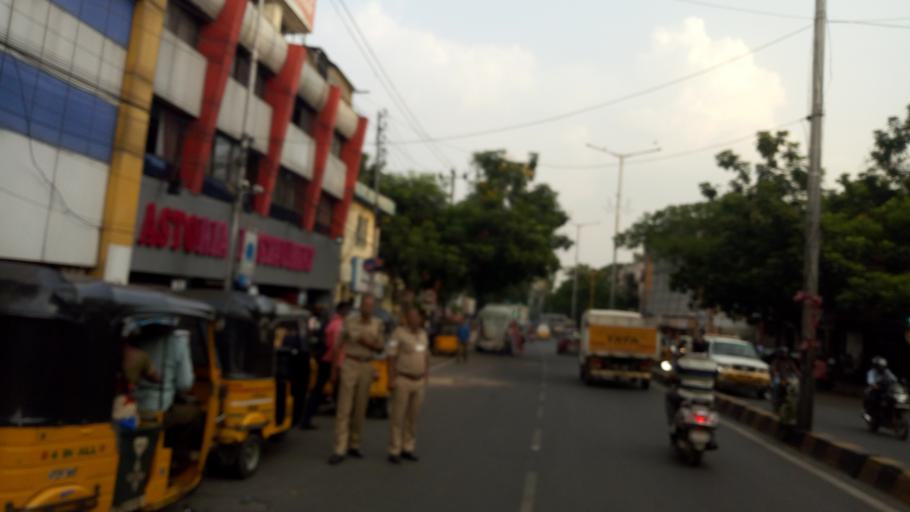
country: IN
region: Telangana
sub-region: Hyderabad
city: Hyderabad
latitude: 17.4048
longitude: 78.4672
